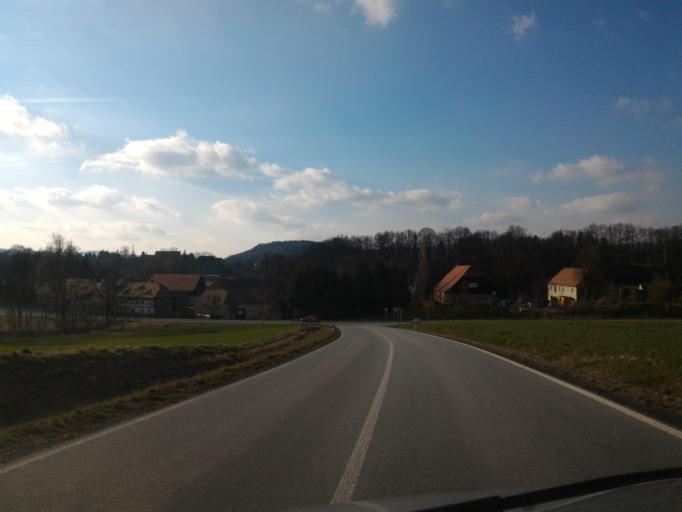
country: DE
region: Saxony
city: Grossschonau
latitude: 50.8921
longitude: 14.6868
